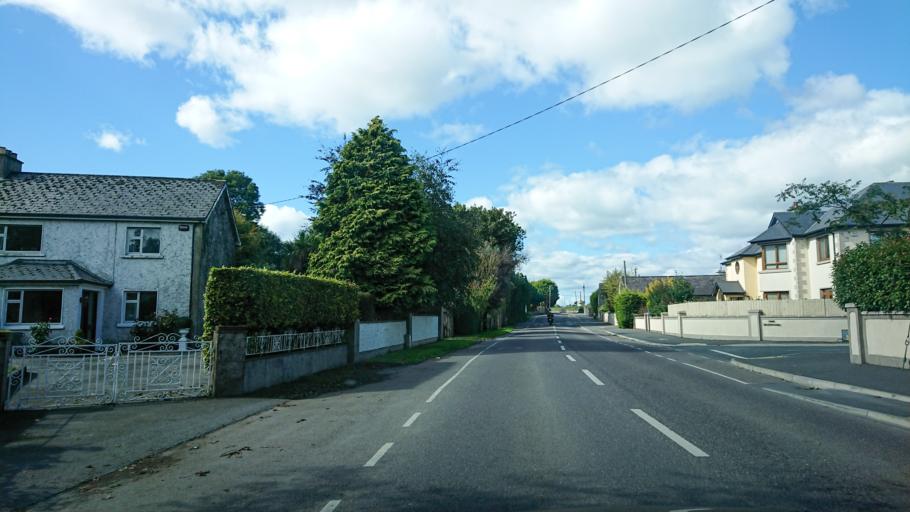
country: IE
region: Munster
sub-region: Waterford
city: Dungarvan
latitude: 52.0939
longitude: -7.6392
